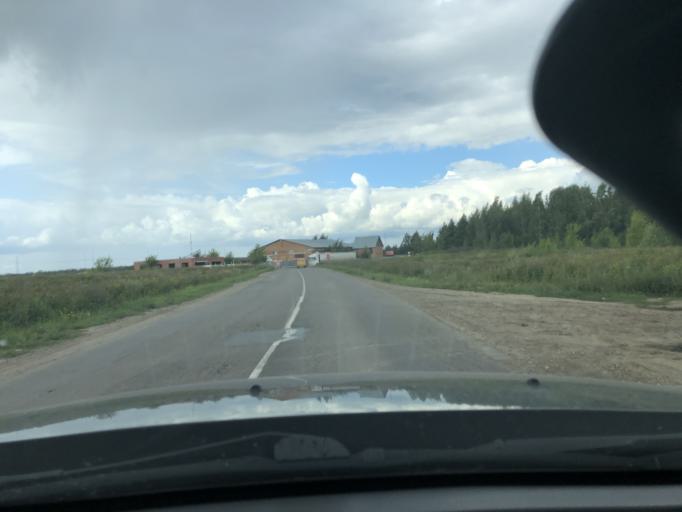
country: RU
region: Tula
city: Kamenetskiy
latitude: 54.0161
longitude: 38.2521
